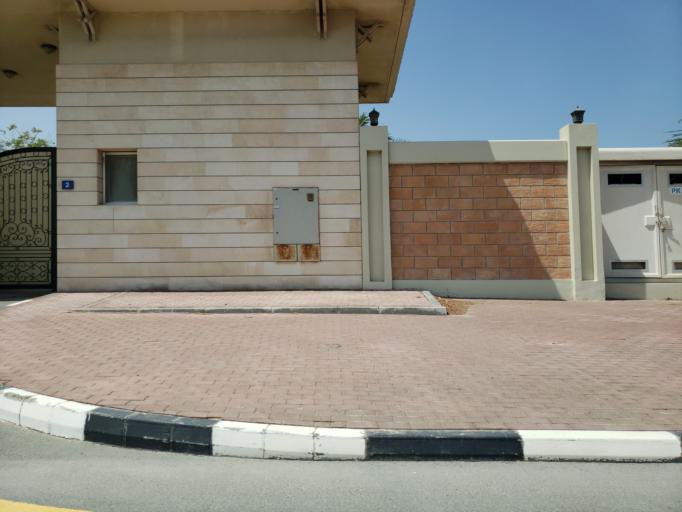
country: AE
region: Dubai
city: Dubai
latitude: 25.1181
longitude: 55.1815
